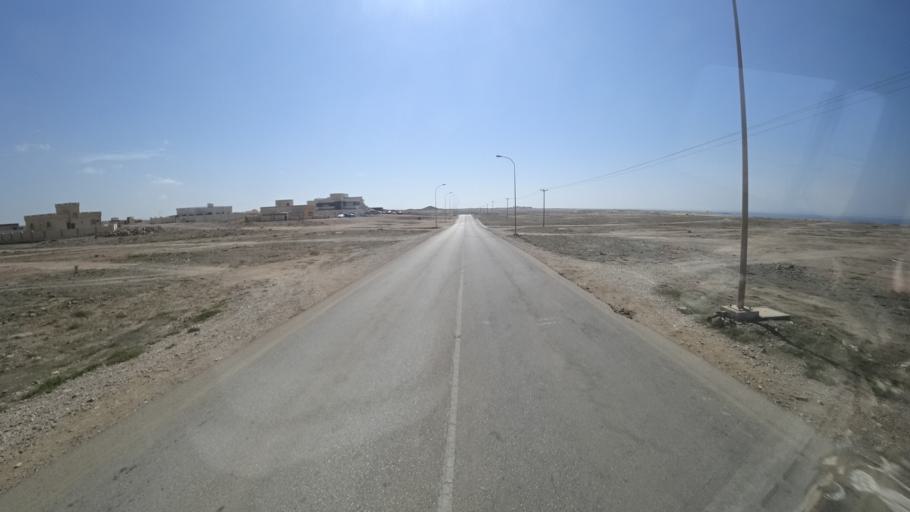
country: OM
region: Zufar
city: Salalah
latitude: 16.9743
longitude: 54.7162
